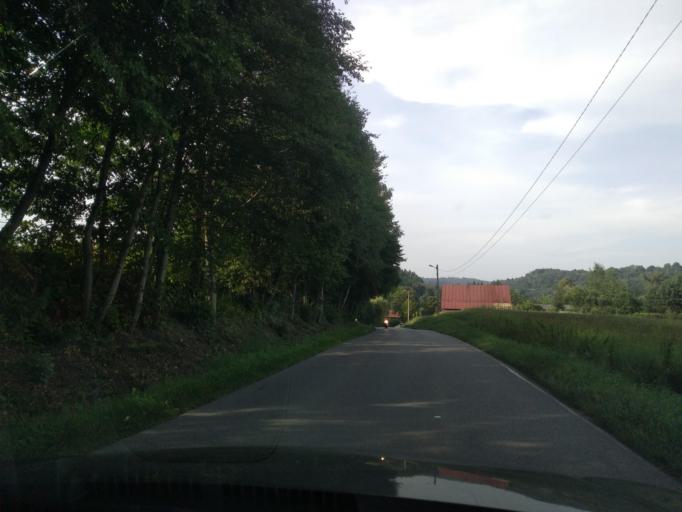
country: PL
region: Subcarpathian Voivodeship
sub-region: Powiat brzozowski
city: Dydnia
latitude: 49.6798
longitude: 22.1845
